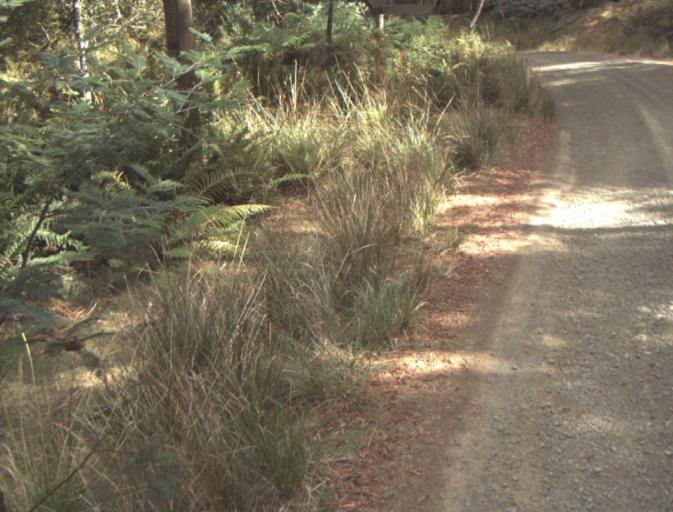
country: AU
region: Tasmania
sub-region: Launceston
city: Mayfield
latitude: -41.2796
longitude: 147.2326
